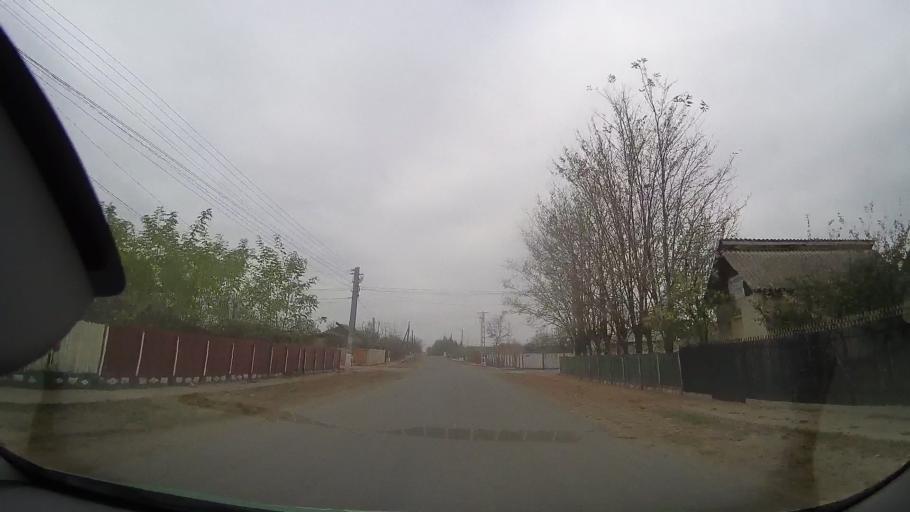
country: RO
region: Buzau
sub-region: Comuna Luciu
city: Luciu
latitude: 44.9730
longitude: 27.0744
